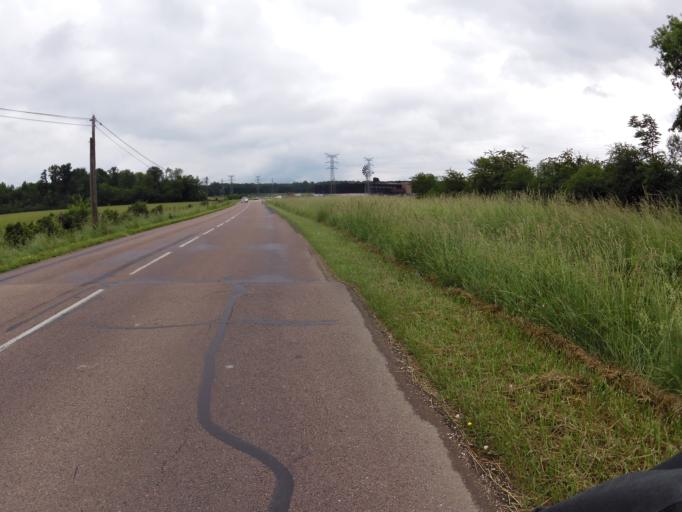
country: FR
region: Champagne-Ardenne
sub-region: Departement de la Haute-Marne
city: Saint-Dizier
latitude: 48.6535
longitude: 4.9361
